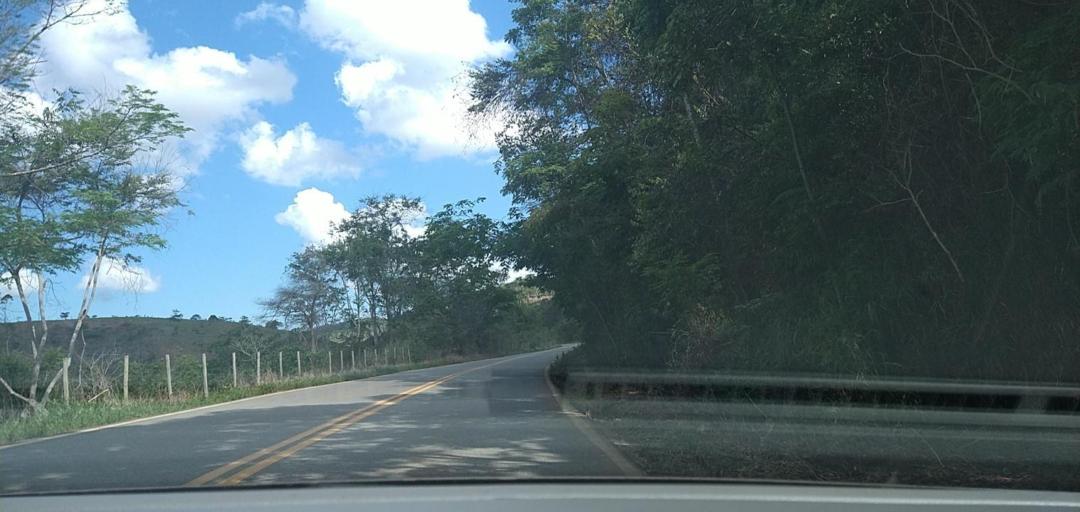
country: BR
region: Minas Gerais
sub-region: Rio Piracicaba
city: Rio Piracicaba
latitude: -19.9973
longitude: -43.1092
